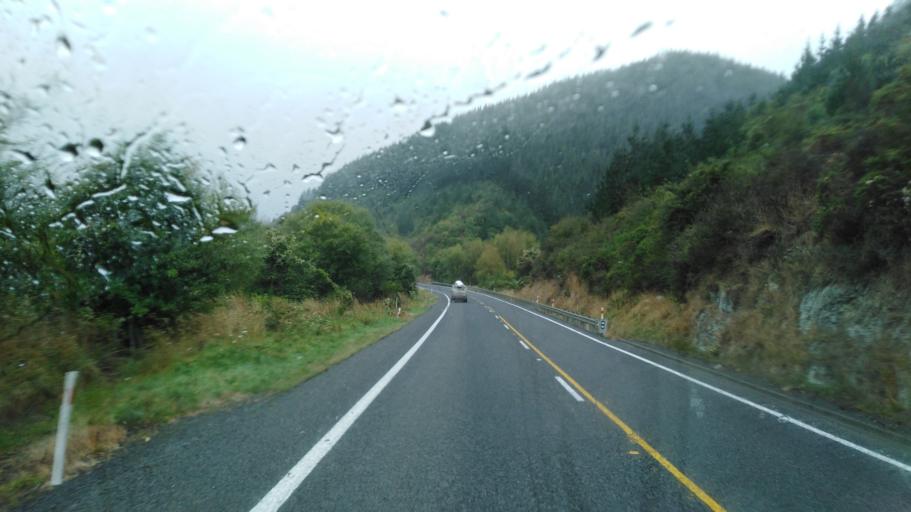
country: NZ
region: Marlborough
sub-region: Marlborough District
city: Picton
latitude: -41.3876
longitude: 173.9520
